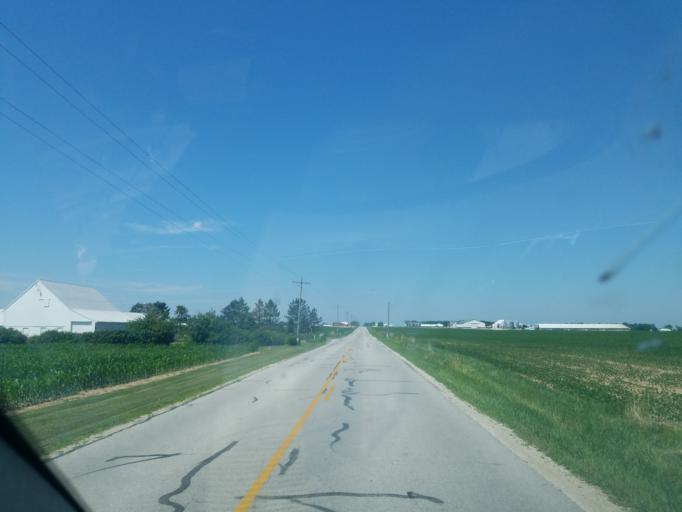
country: US
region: Ohio
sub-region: Mercer County
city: Saint Henry
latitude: 40.4506
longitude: -84.6775
